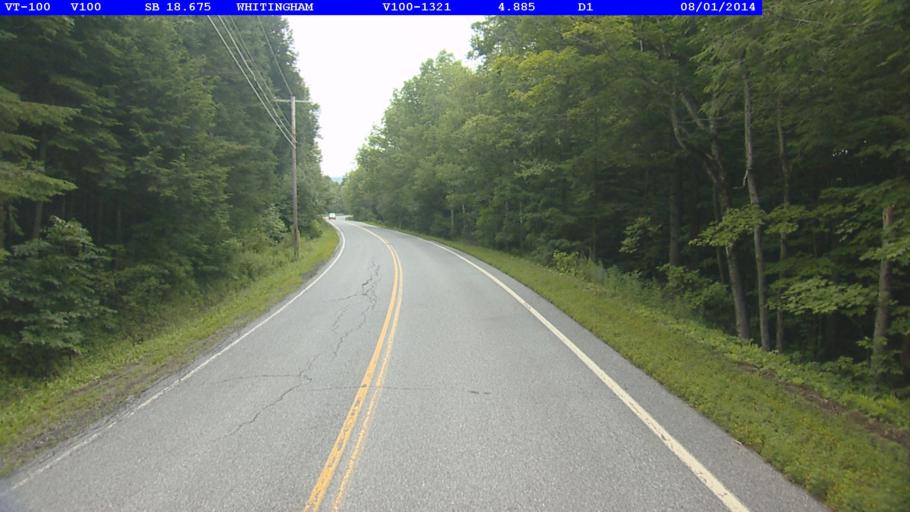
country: US
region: Massachusetts
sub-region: Franklin County
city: Charlemont
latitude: 42.7901
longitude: -72.8693
